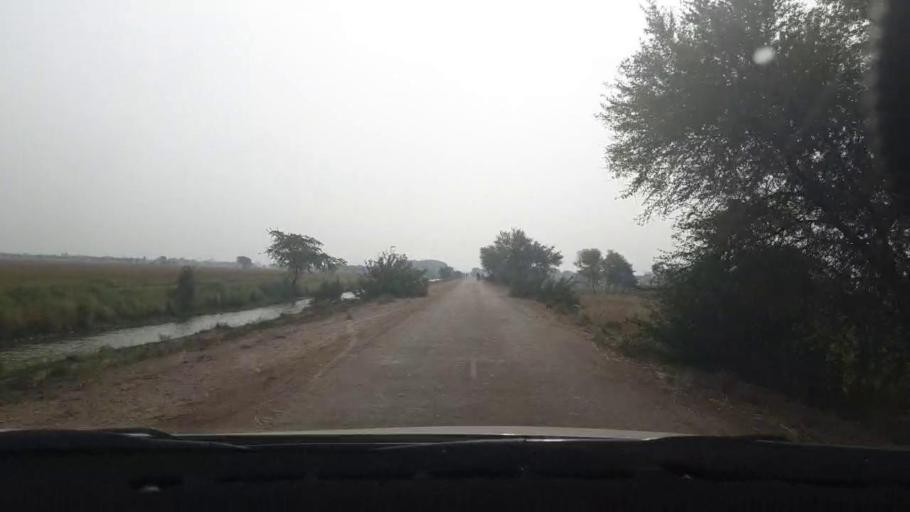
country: PK
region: Sindh
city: Tando Muhammad Khan
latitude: 25.0633
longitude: 68.5423
